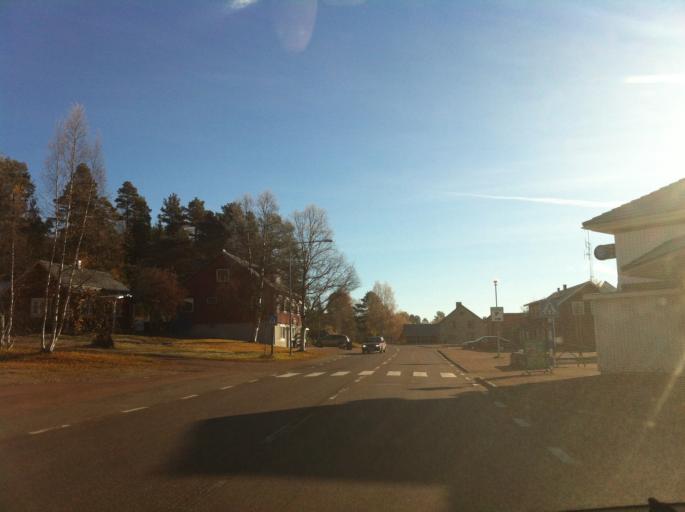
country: NO
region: Hedmark
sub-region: Trysil
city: Innbygda
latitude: 61.8579
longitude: 12.7264
